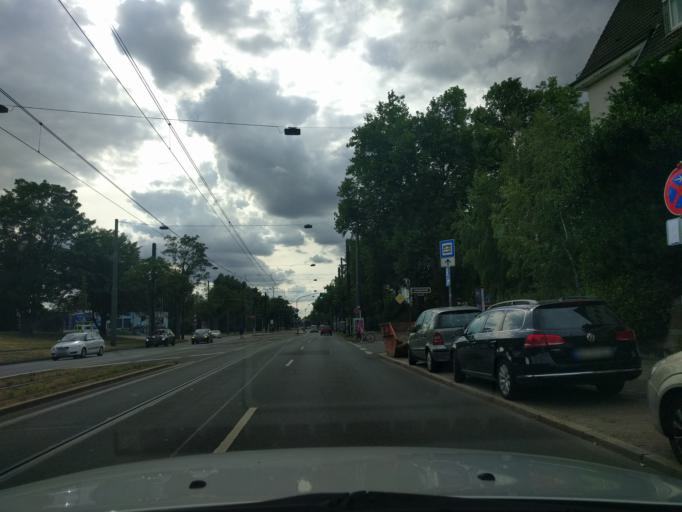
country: DE
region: North Rhine-Westphalia
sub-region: Regierungsbezirk Dusseldorf
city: Dusseldorf
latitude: 51.2306
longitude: 6.7407
